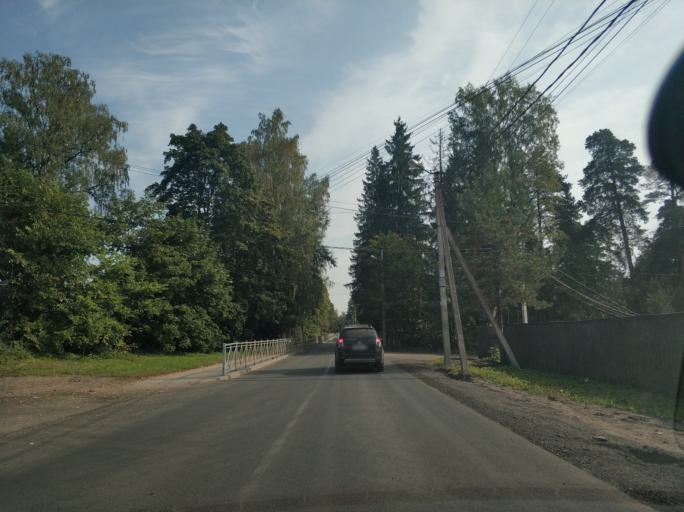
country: RU
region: Leningrad
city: Vsevolozhsk
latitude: 60.0197
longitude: 30.6705
